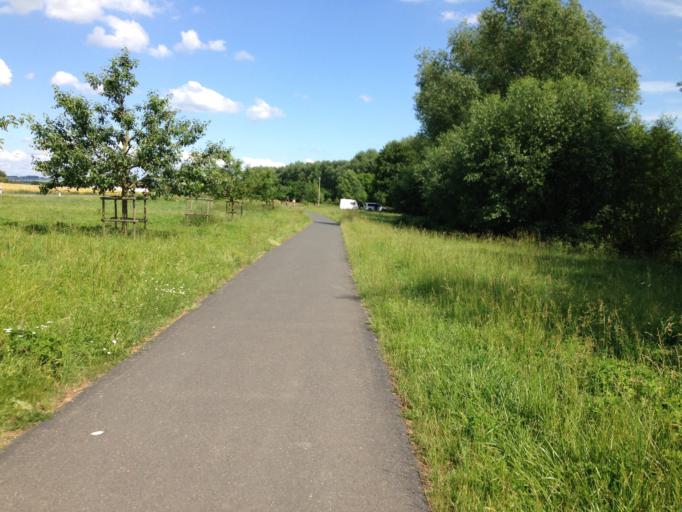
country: DE
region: Hesse
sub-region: Regierungsbezirk Giessen
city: Hoernsheim
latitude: 50.5161
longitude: 8.6049
